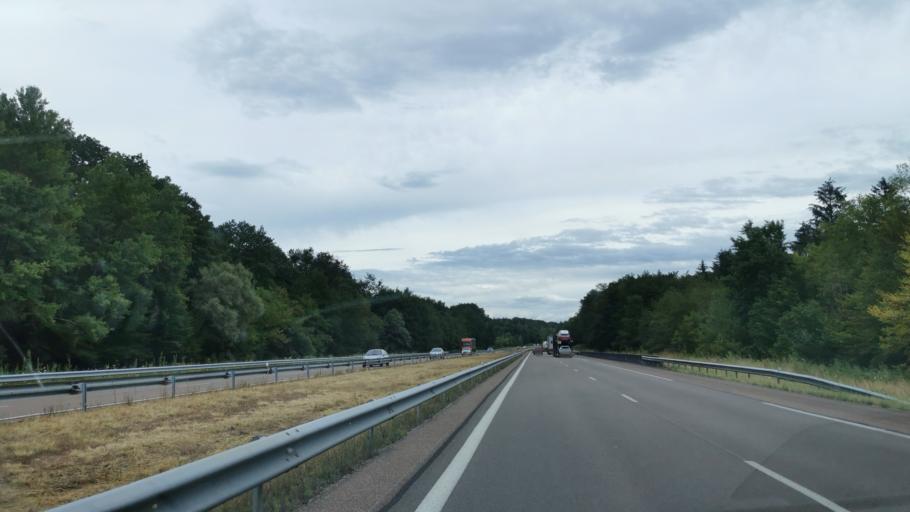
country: FR
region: Franche-Comte
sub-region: Departement du Jura
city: Bletterans
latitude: 46.6856
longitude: 5.4458
